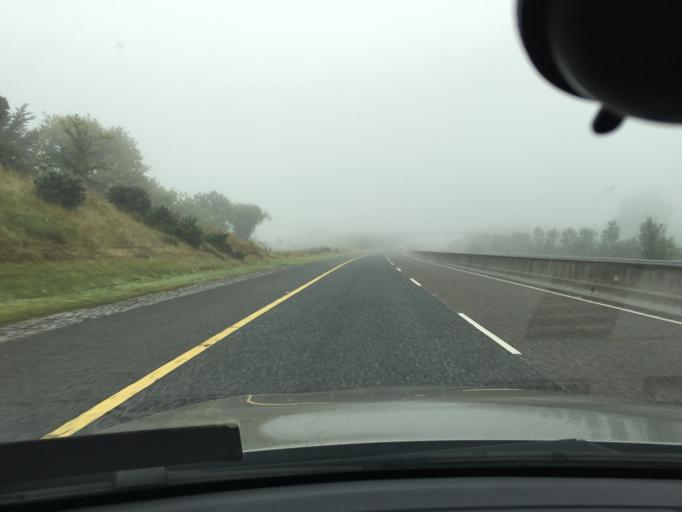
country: IE
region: Leinster
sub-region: Uibh Fhaili
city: Clara
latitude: 53.3866
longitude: -7.5991
